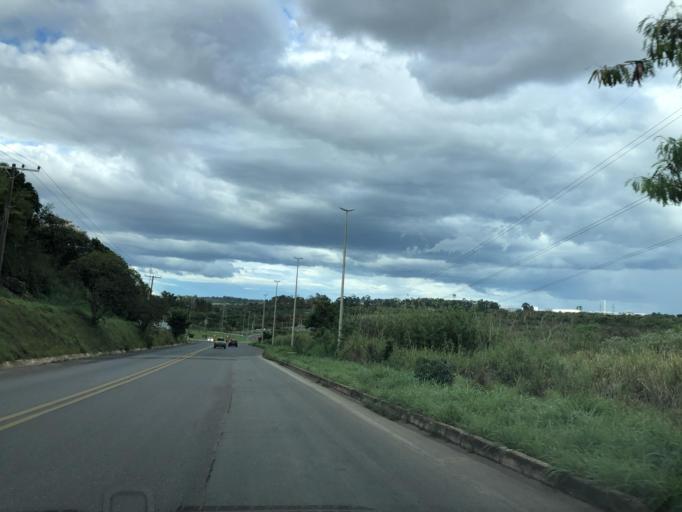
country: BR
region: Goias
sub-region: Luziania
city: Luziania
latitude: -16.0412
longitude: -48.0570
